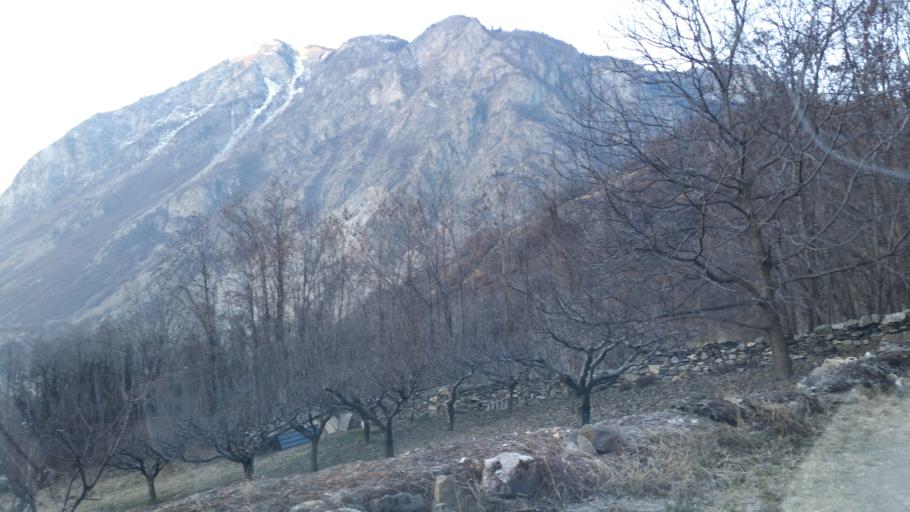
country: FR
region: Rhone-Alpes
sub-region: Departement de la Savoie
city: Saint-Jean-de-Maurienne
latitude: 45.3004
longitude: 6.3617
